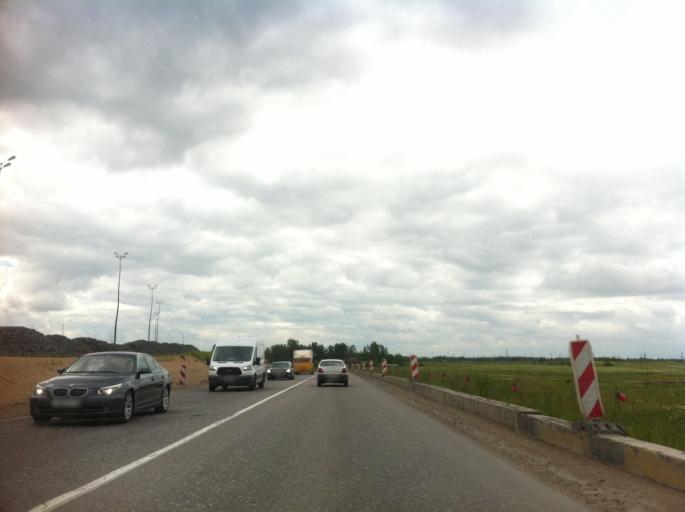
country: RU
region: Leningrad
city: Maloye Verevo
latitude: 59.6694
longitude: 30.2305
